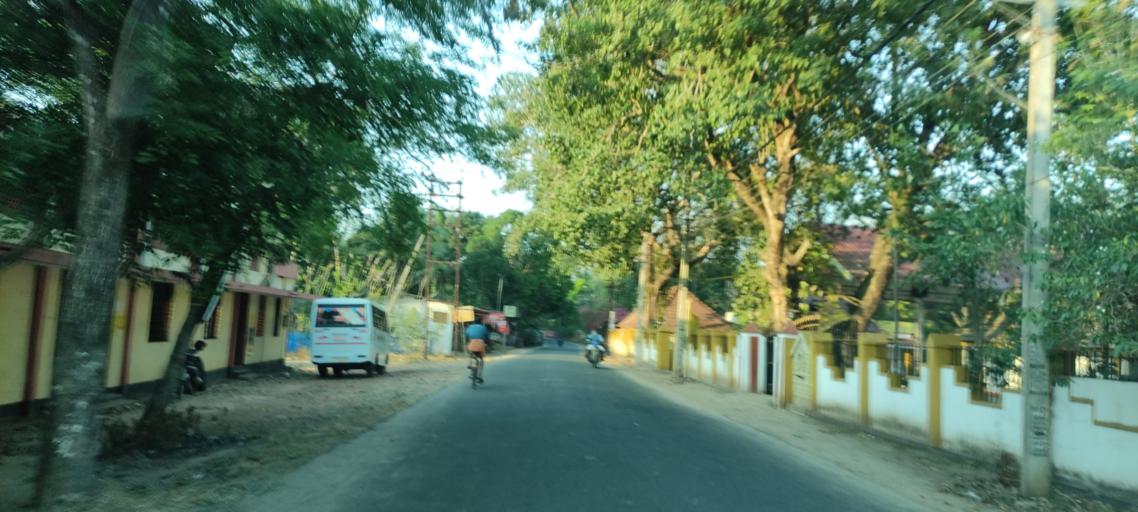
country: IN
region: Kerala
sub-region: Kottayam
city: Vaikam
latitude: 9.7578
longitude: 76.3535
